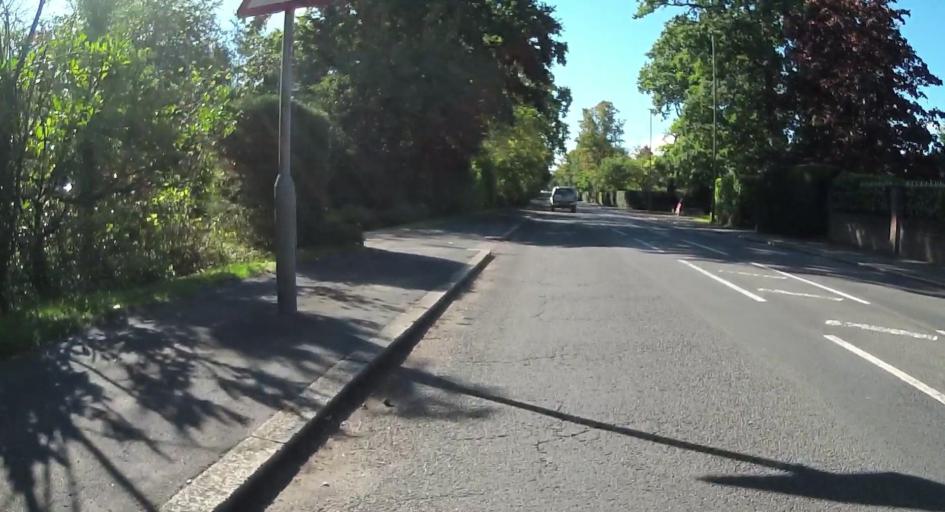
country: GB
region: England
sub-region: Surrey
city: Walton-on-Thames
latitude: 51.3771
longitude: -0.4203
